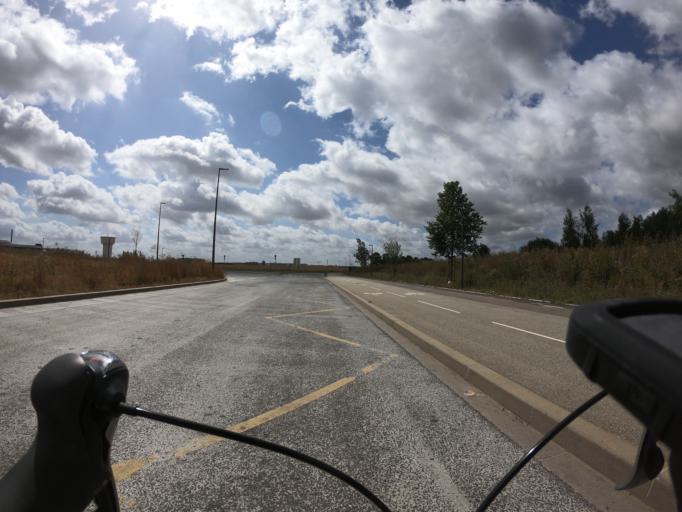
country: FR
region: Ile-de-France
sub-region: Departement de l'Essonne
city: Saclay
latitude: 48.7294
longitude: 2.1611
